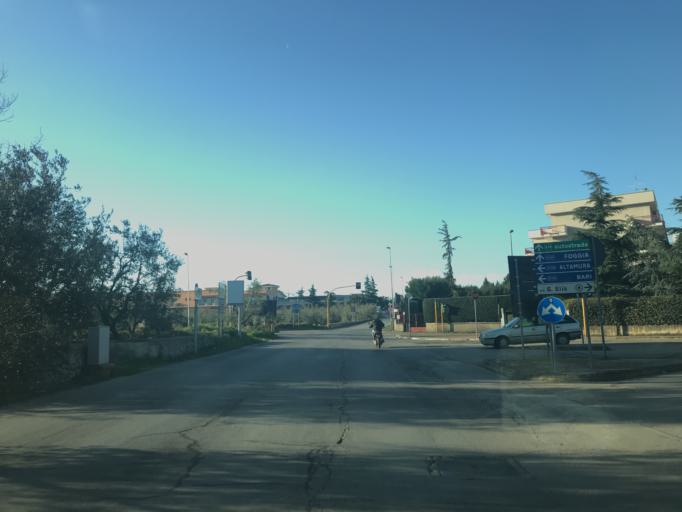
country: IT
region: Apulia
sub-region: Provincia di Bari
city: Corato
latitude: 41.1389
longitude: 16.4153
